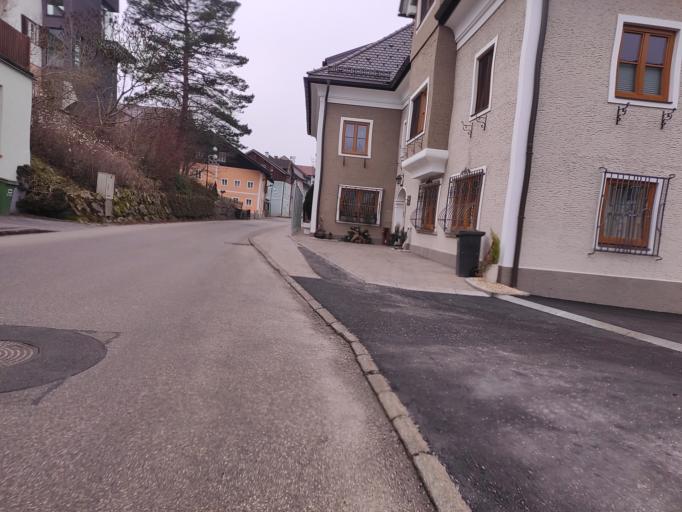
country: AT
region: Salzburg
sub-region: Politischer Bezirk Salzburg-Umgebung
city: Kostendorf
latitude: 47.9570
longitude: 13.2005
